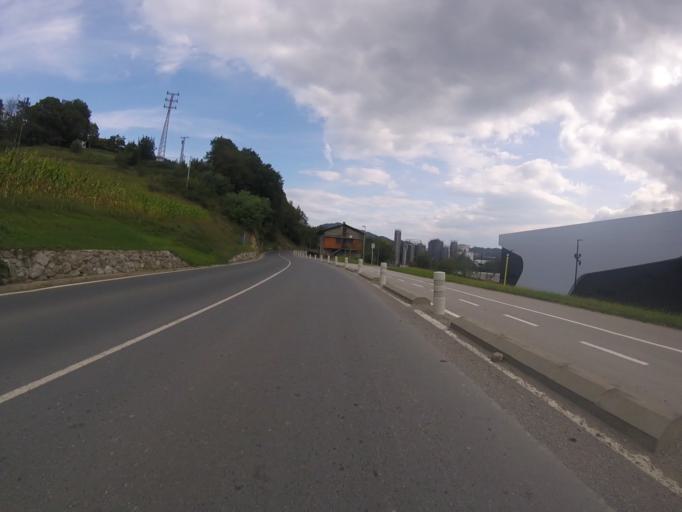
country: ES
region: Basque Country
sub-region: Provincia de Guipuzcoa
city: Aduna
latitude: 43.2058
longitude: -2.0408
